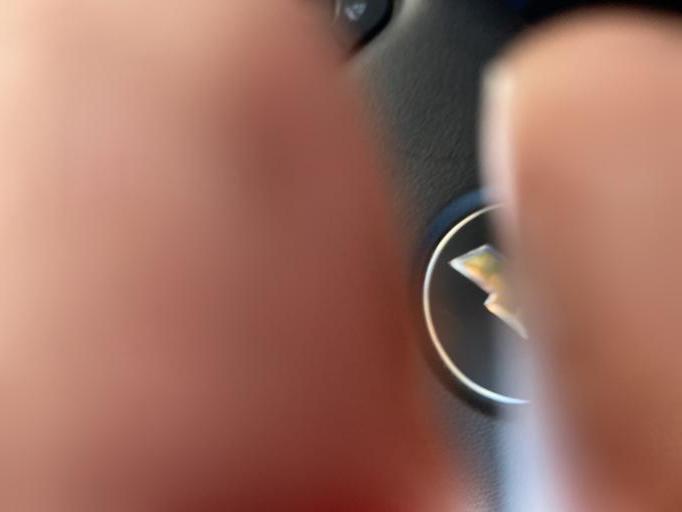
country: US
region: California
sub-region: Sacramento County
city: Elk Grove
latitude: 38.4077
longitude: -121.3851
